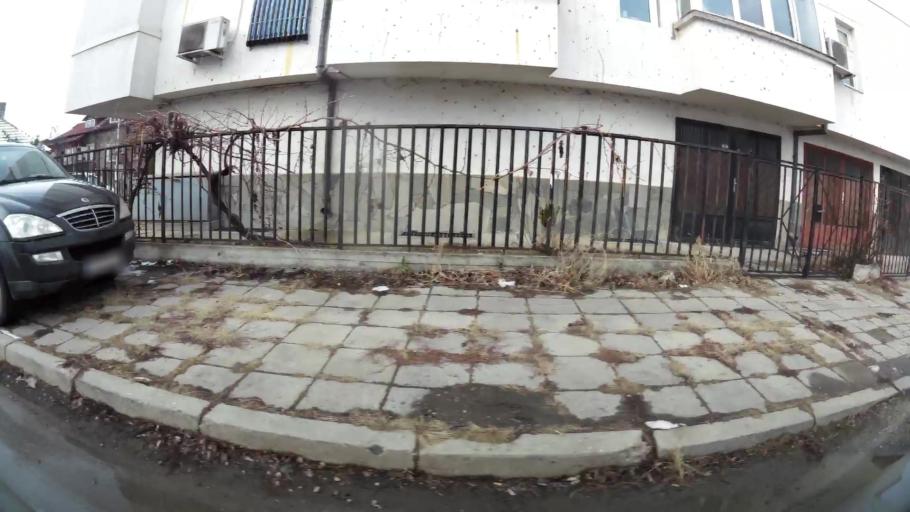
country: BG
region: Sofia-Capital
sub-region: Stolichna Obshtina
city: Sofia
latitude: 42.6998
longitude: 23.3805
